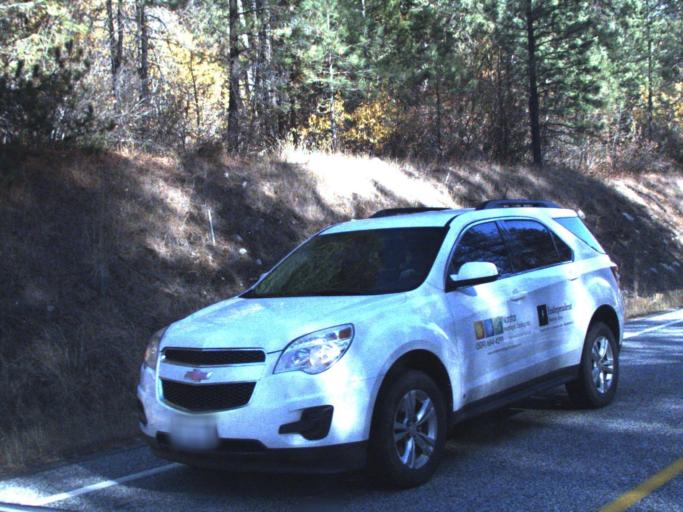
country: US
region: Washington
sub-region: Stevens County
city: Kettle Falls
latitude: 48.5855
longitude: -118.2015
